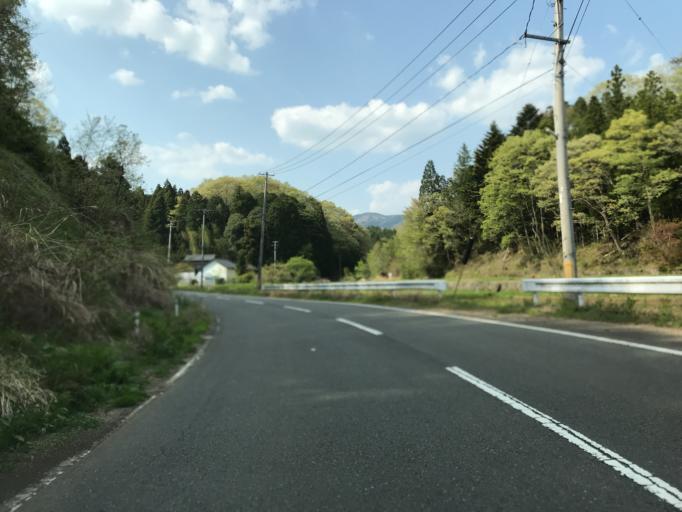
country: JP
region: Fukushima
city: Iwaki
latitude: 36.9985
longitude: 140.7738
